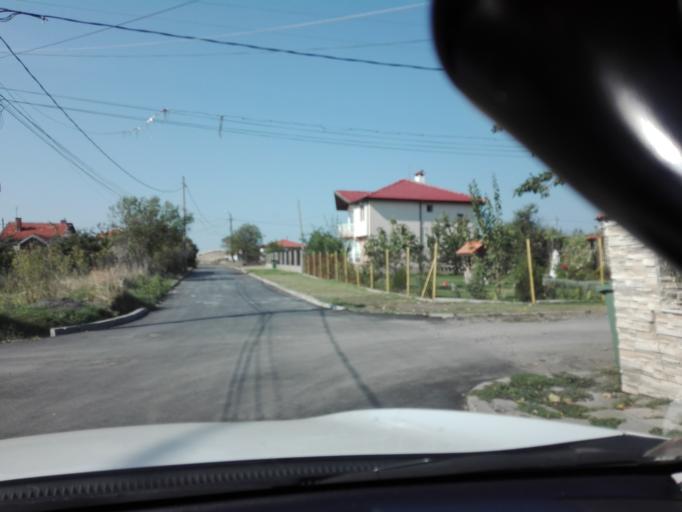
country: BG
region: Burgas
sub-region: Obshtina Kameno
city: Kameno
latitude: 42.6259
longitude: 27.3889
